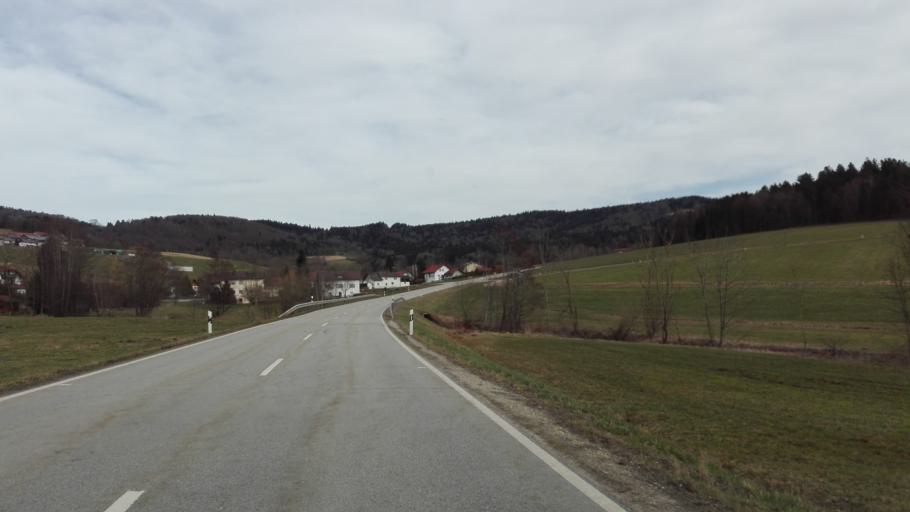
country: DE
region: Bavaria
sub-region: Lower Bavaria
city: Hauzenberg
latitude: 48.6328
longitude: 13.6672
